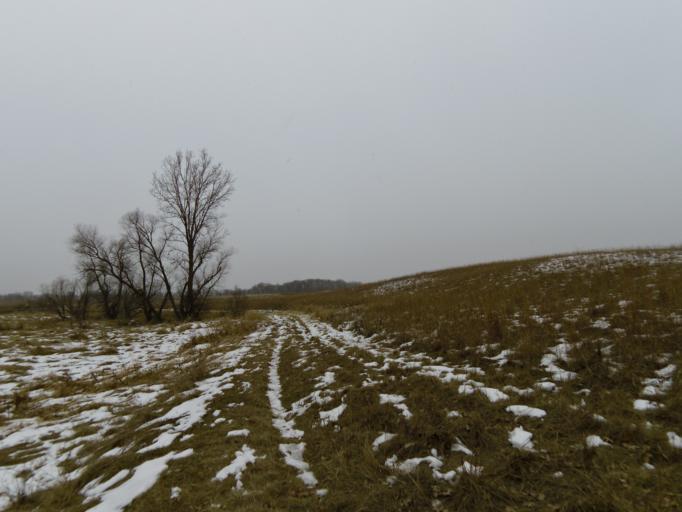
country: US
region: Minnesota
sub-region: Washington County
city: Lake Elmo
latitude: 44.9849
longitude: -92.9121
